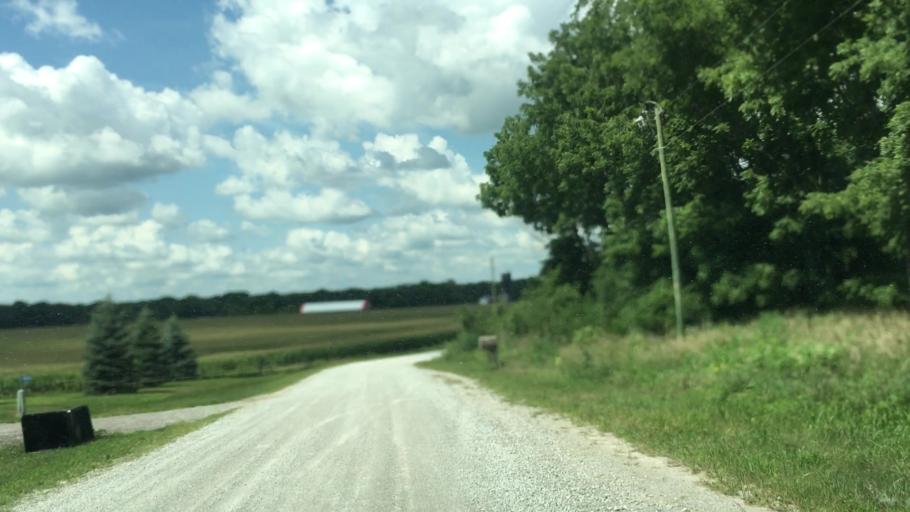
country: US
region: Iowa
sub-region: Linn County
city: Lisbon
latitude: 41.8284
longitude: -91.3861
